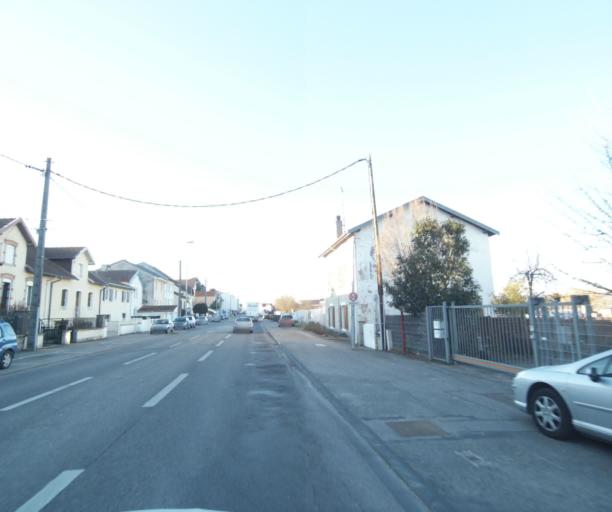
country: FR
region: Lorraine
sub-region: Departement de Meurthe-et-Moselle
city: Heillecourt
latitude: 48.6635
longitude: 6.2191
